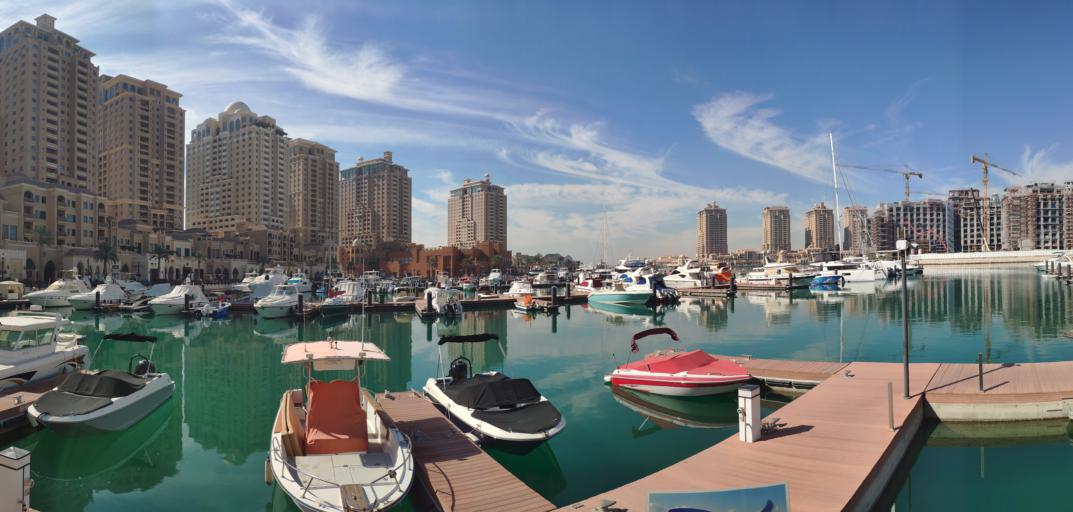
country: QA
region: Baladiyat ad Dawhah
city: Doha
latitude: 25.3680
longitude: 51.5474
